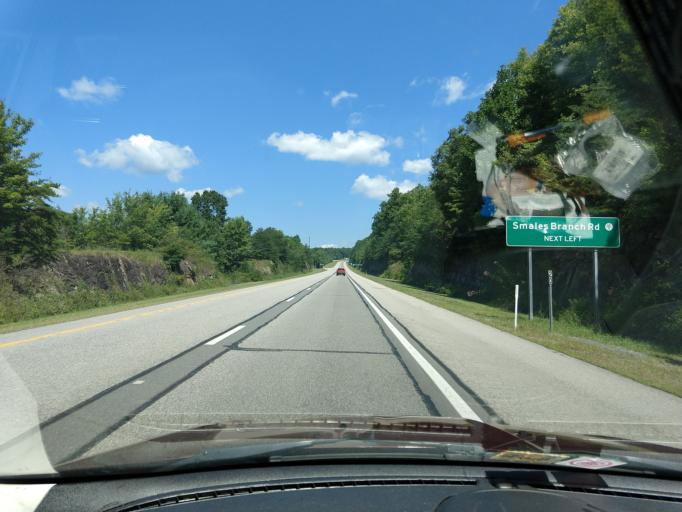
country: US
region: West Virginia
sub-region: Fayette County
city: Ansted
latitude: 38.1081
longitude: -81.0170
